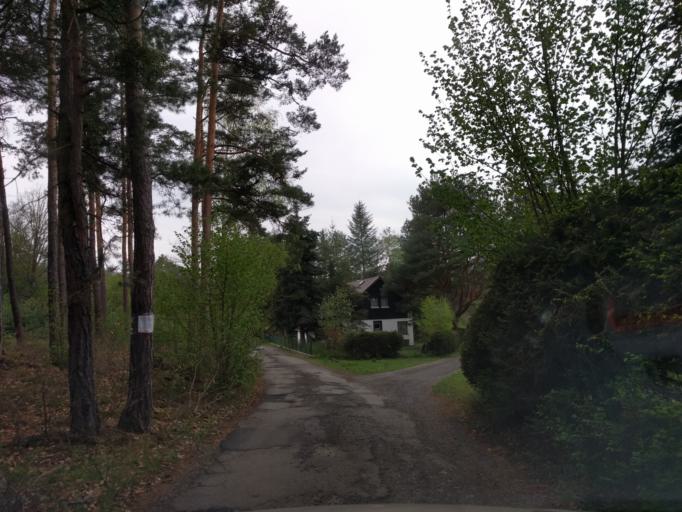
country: CZ
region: Central Bohemia
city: Krasna Hora nad Vltavou
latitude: 49.6665
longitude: 14.2598
